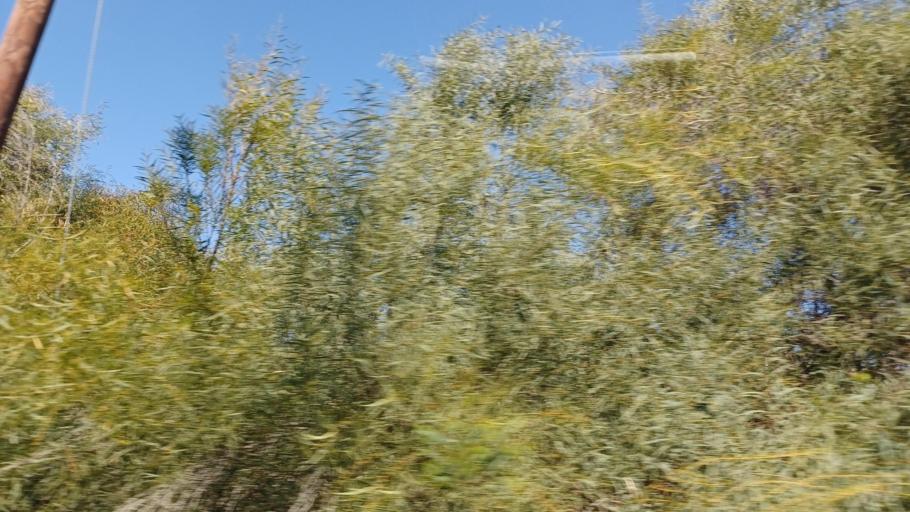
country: CY
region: Limassol
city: Parekklisha
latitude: 34.7523
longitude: 33.1368
